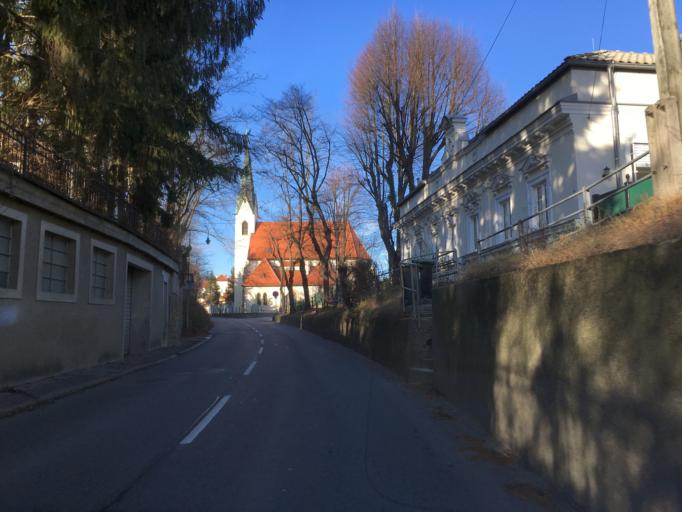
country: AT
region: Lower Austria
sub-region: Politischer Bezirk Wien-Umgebung
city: Klosterneuburg
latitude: 48.3269
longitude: 16.3029
